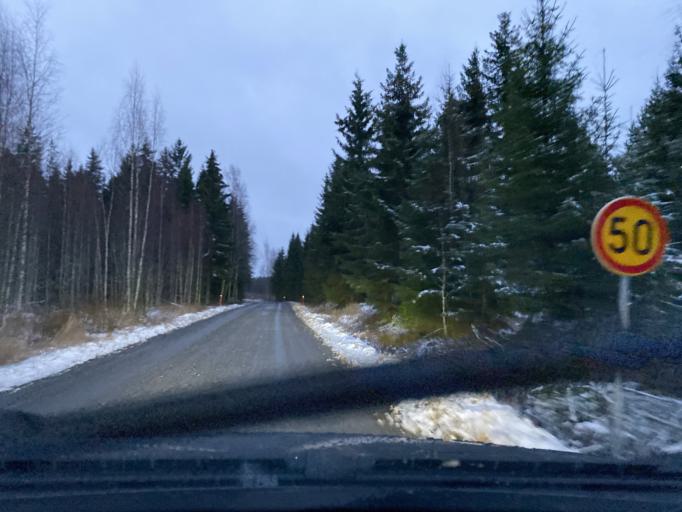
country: FI
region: Pirkanmaa
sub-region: Lounais-Pirkanmaa
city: Punkalaidun
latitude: 61.1578
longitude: 22.9610
